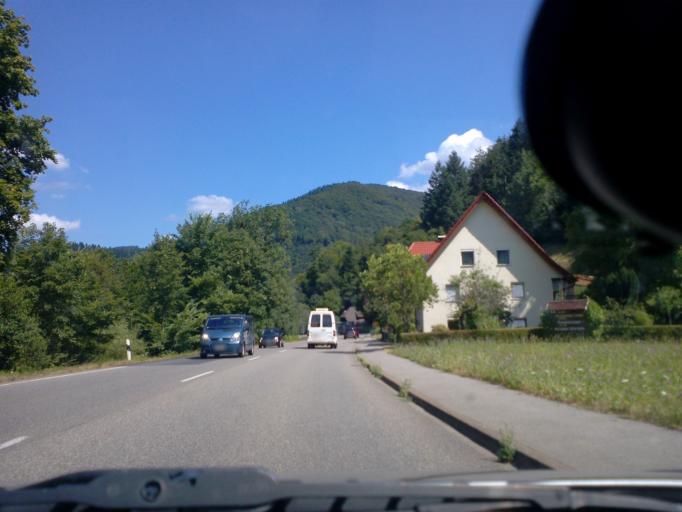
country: DE
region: Baden-Wuerttemberg
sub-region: Freiburg Region
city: Hausach
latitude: 48.2781
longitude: 8.1972
